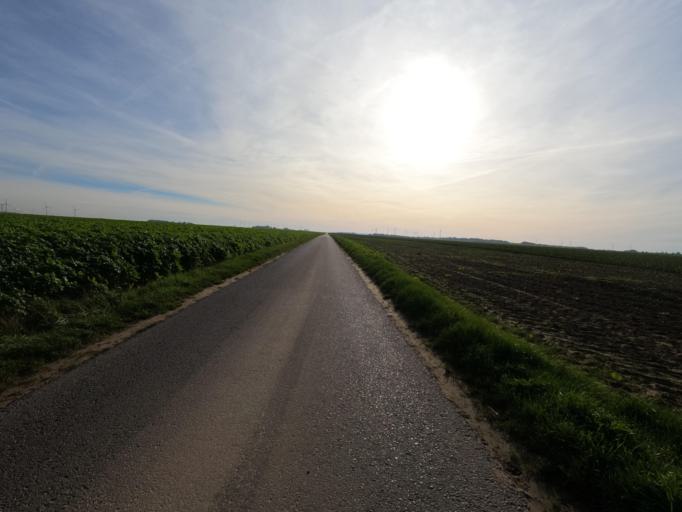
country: DE
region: North Rhine-Westphalia
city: Erkelenz
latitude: 51.0739
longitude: 6.3684
